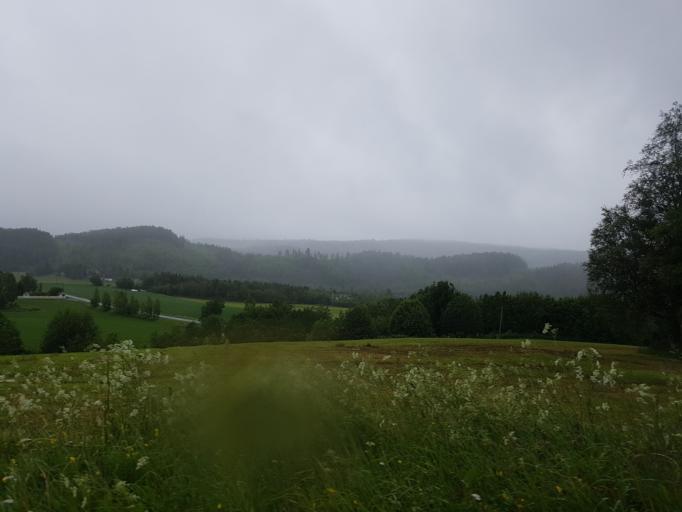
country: NO
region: Nord-Trondelag
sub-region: Stjordal
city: Stjordalshalsen
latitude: 63.3930
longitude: 11.0663
